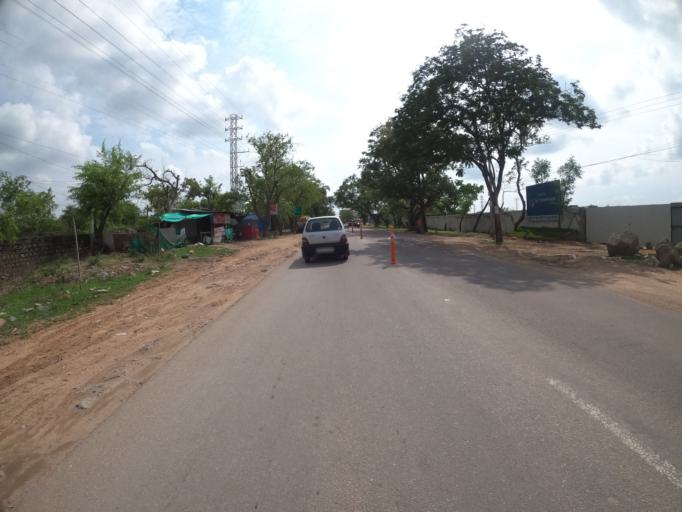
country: IN
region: Telangana
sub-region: Medak
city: Serilingampalle
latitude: 17.3855
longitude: 78.3322
